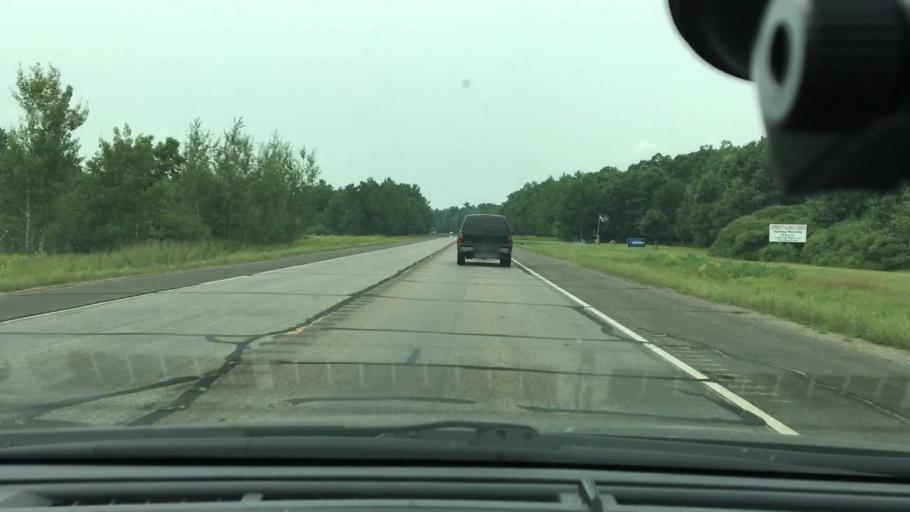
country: US
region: Minnesota
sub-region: Mille Lacs County
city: Vineland
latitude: 46.3208
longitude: -93.8031
